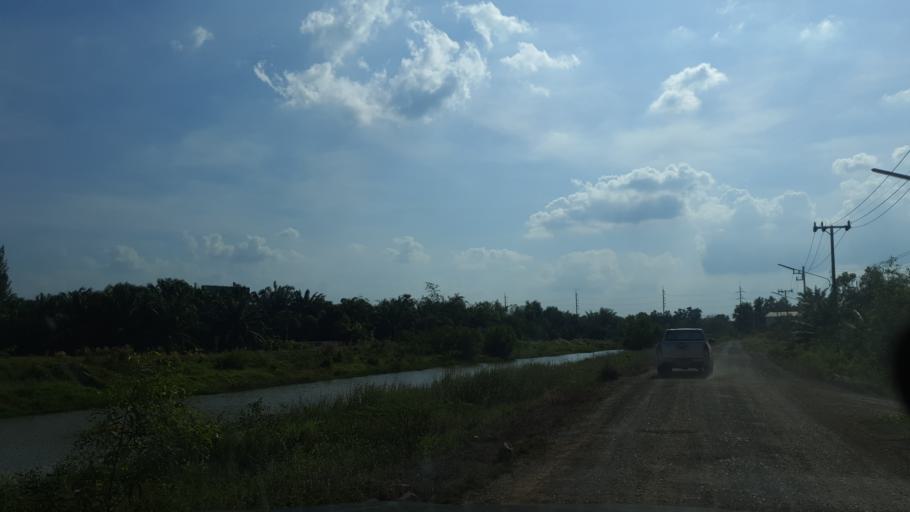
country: TH
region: Surat Thani
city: Phunphin
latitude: 9.1436
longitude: 99.1595
